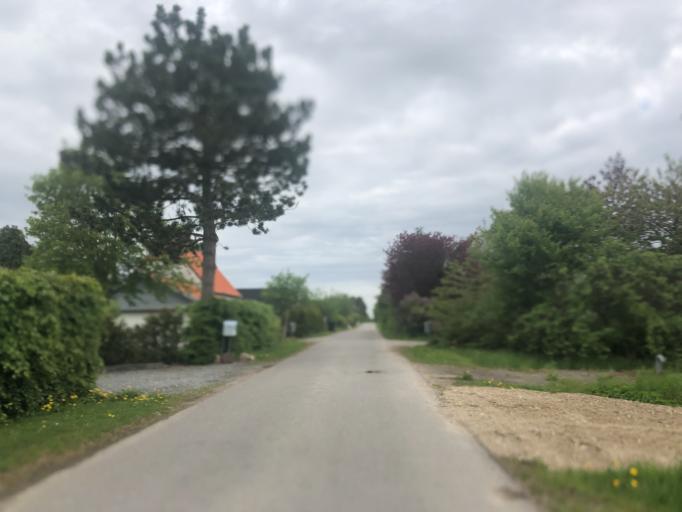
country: DK
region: Zealand
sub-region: Koge Kommune
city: Ejby
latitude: 55.4525
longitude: 12.0996
